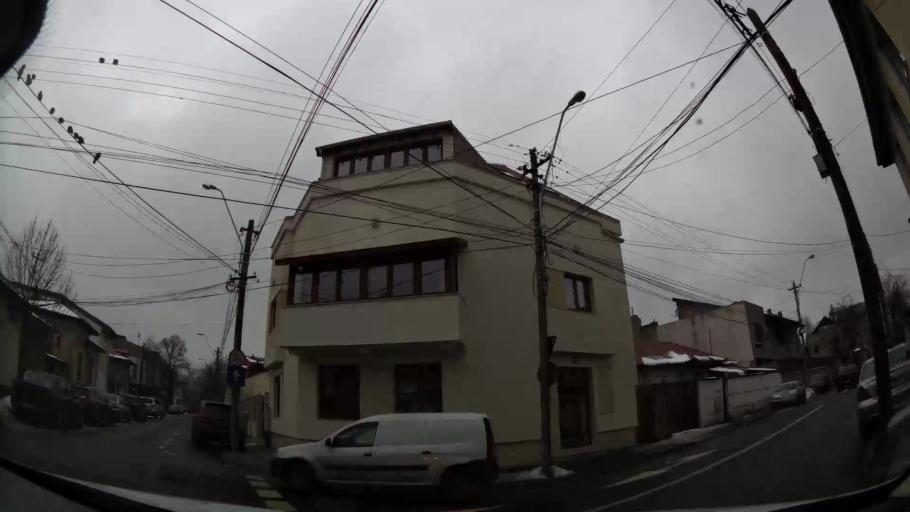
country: RO
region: Bucuresti
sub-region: Municipiul Bucuresti
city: Bucuresti
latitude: 44.4608
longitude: 26.0686
